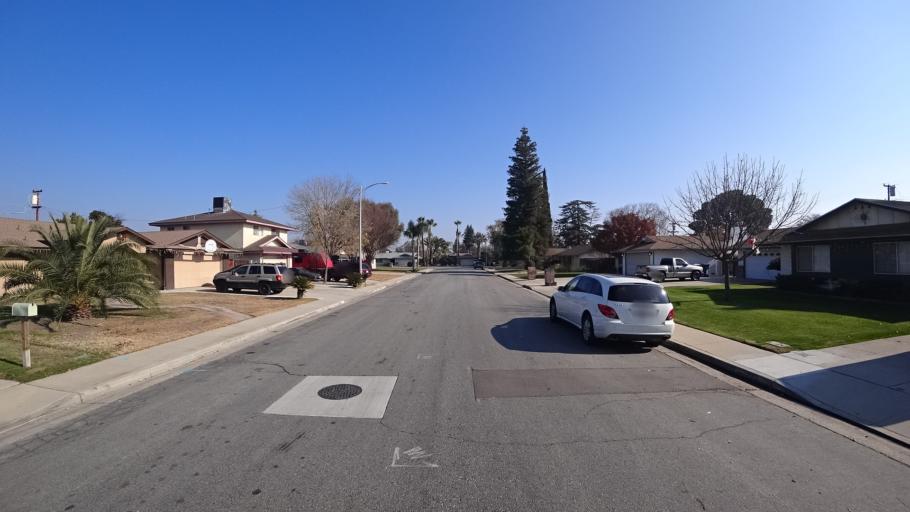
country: US
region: California
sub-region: Kern County
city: Greenacres
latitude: 35.3560
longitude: -119.0672
